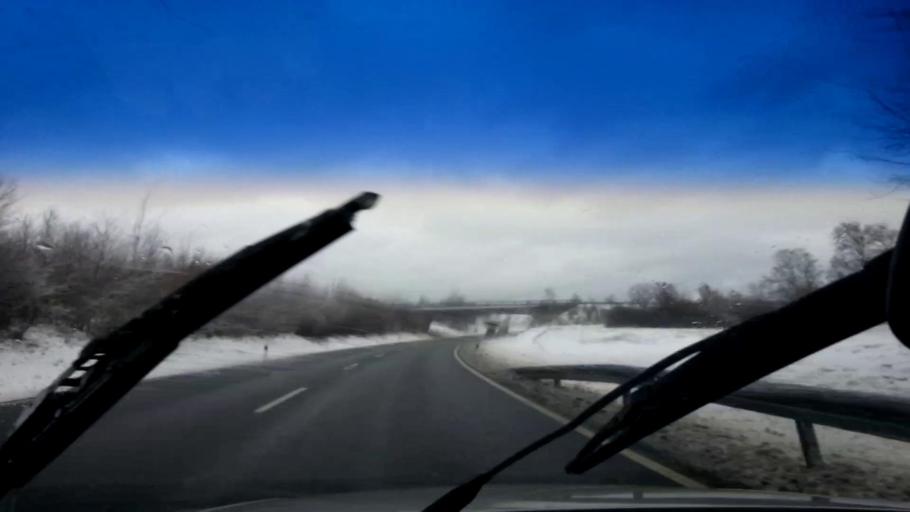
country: DE
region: Bavaria
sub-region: Upper Franconia
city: Selb
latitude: 50.1925
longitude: 12.1303
